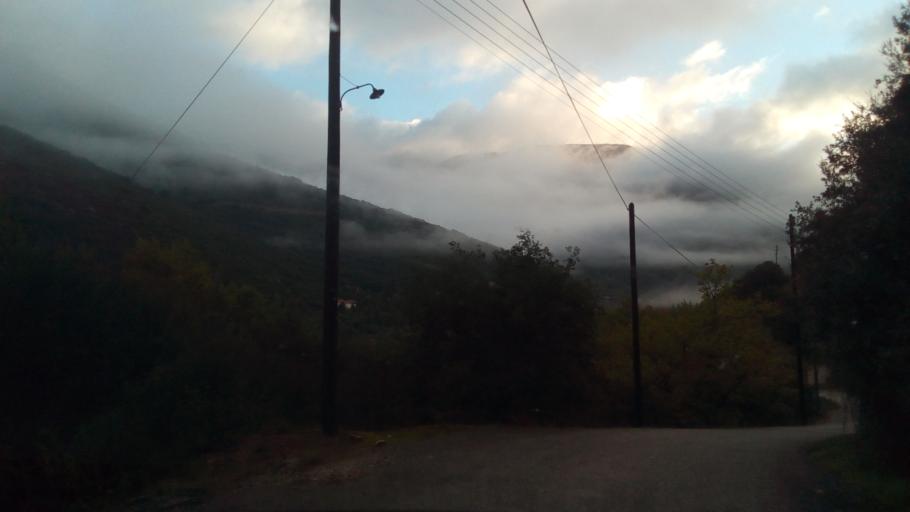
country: GR
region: West Greece
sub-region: Nomos Aitolias kai Akarnanias
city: Thermo
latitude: 38.5144
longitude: 21.7629
